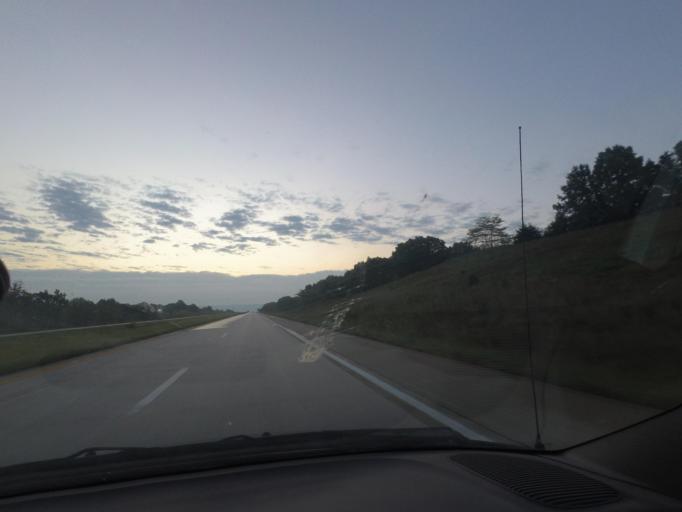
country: US
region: Missouri
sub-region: Macon County
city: Macon
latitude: 39.7588
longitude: -92.6570
